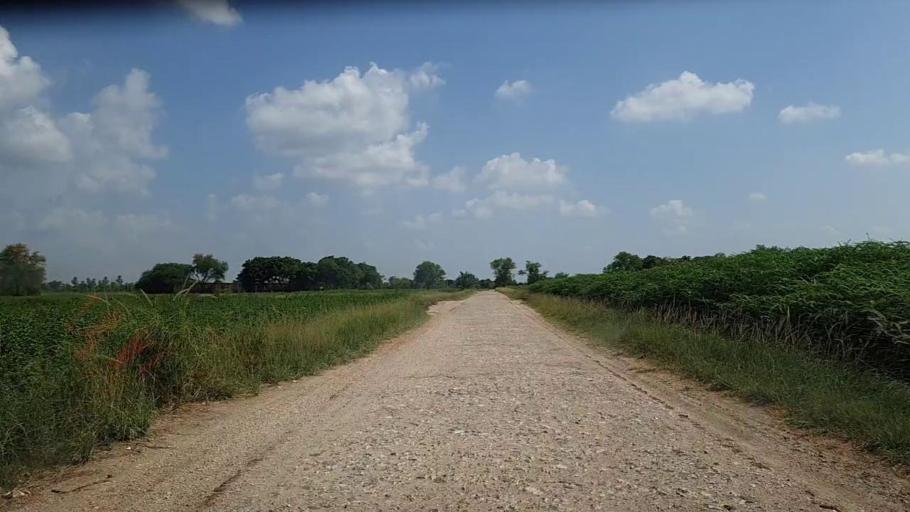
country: PK
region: Sindh
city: Kandiaro
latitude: 26.9971
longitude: 68.3053
